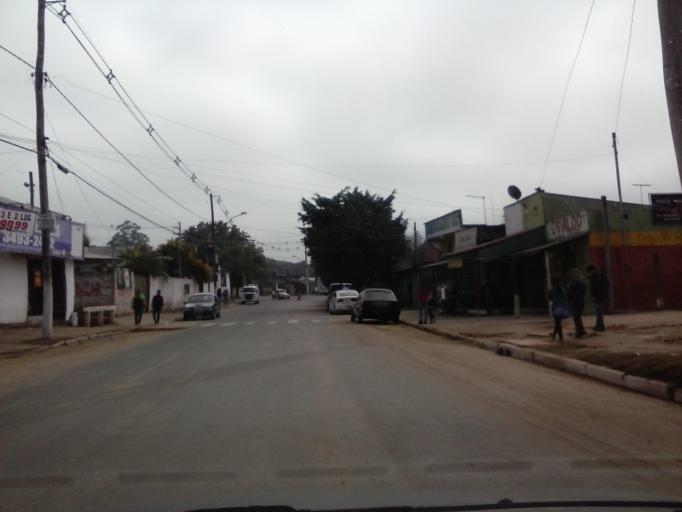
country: BR
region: Rio Grande do Sul
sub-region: Viamao
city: Viamao
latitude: -30.0482
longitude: -51.0846
